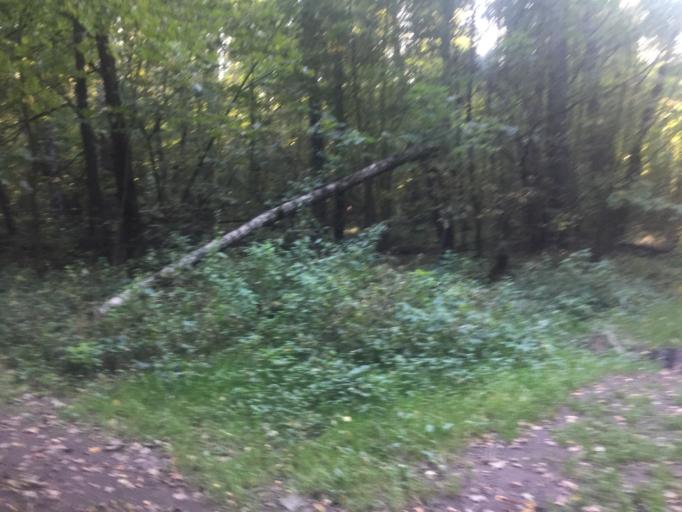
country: RU
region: Moscow
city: Gol'yanovo
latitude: 55.8397
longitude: 37.7974
